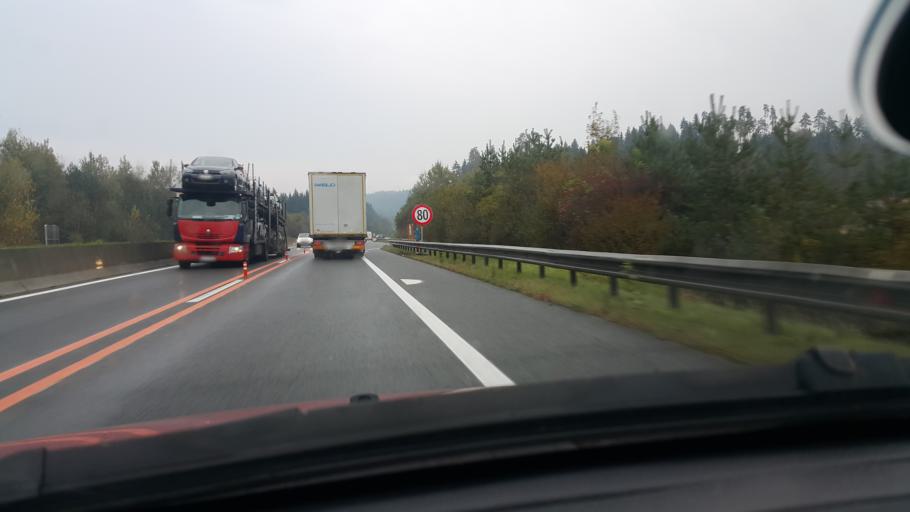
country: AT
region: Carinthia
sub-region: Politischer Bezirk Klagenfurt Land
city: Grafenstein
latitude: 46.6485
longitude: 14.5429
